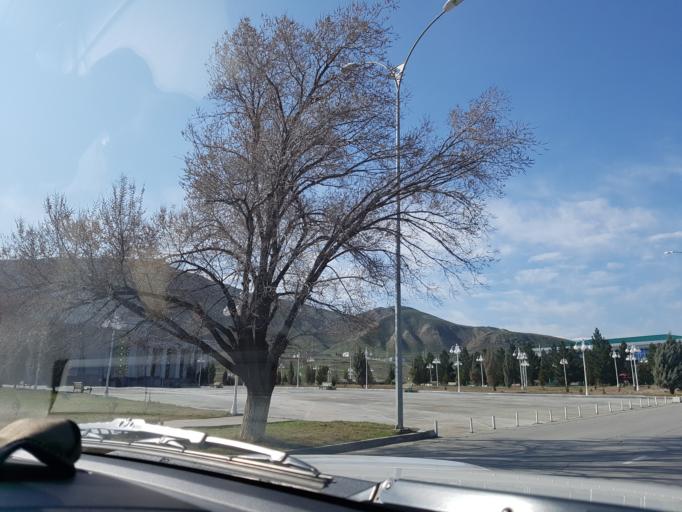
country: TM
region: Ahal
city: Baharly
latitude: 38.5177
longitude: 57.1810
